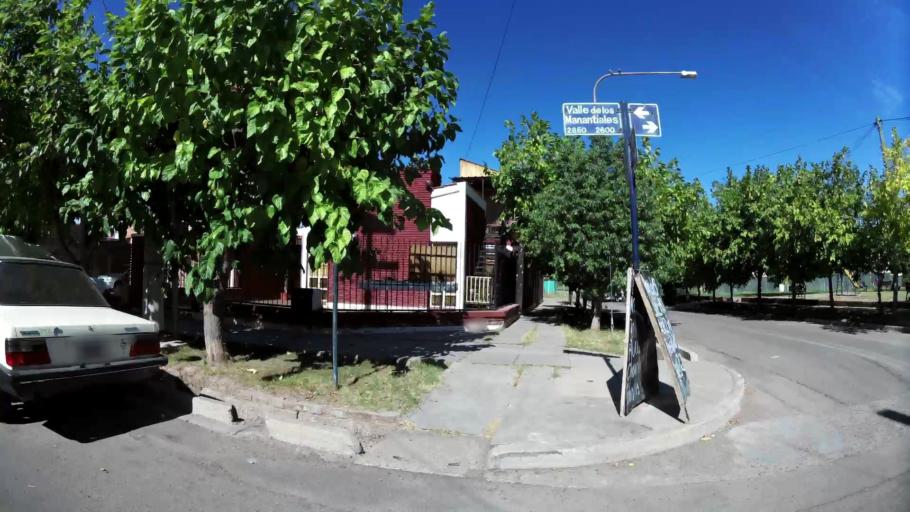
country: AR
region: Mendoza
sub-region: Departamento de Godoy Cruz
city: Godoy Cruz
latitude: -32.9477
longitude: -68.8121
